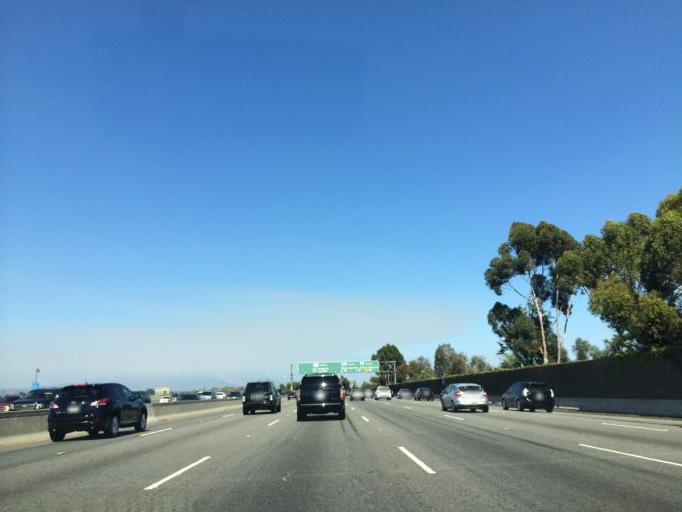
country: US
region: California
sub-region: Los Angeles County
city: Sherman Oaks
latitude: 34.1653
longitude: -118.4799
